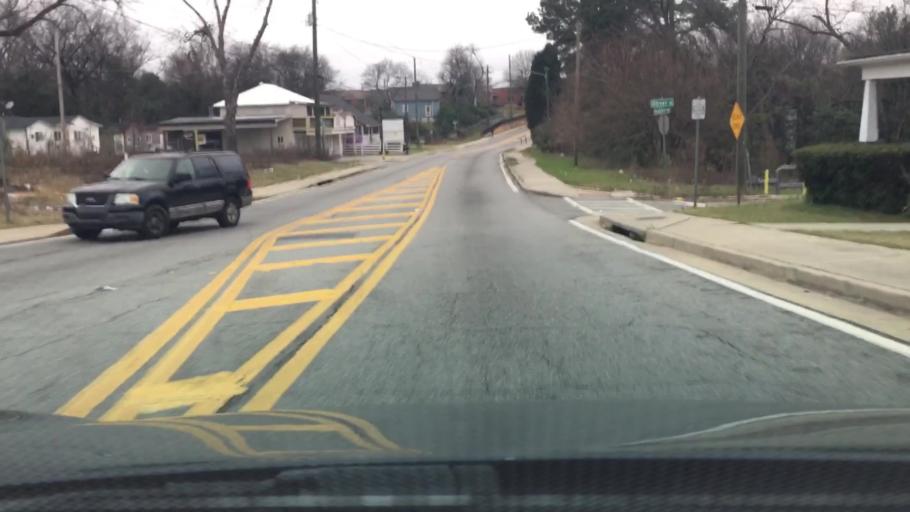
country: US
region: Georgia
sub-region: Bibb County
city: Macon
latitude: 32.8145
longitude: -83.6446
